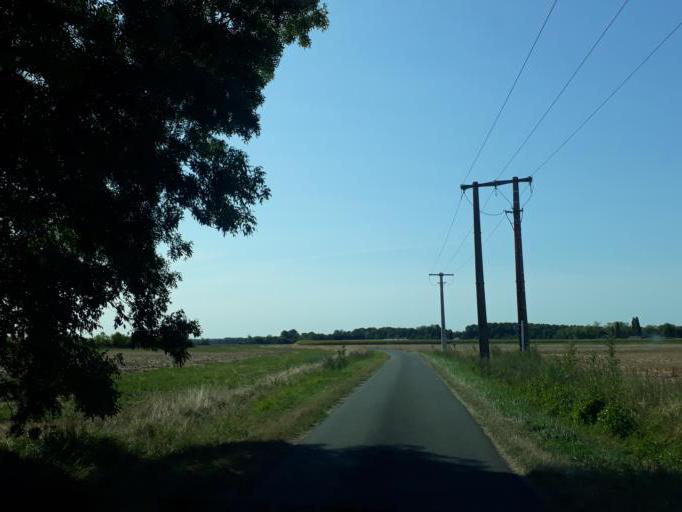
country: FR
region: Centre
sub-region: Departement du Loir-et-Cher
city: Selles-sur-Cher
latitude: 47.2686
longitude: 1.5857
